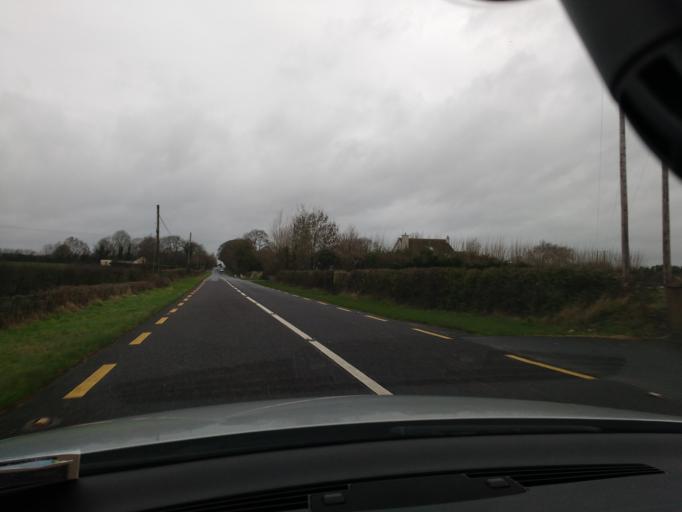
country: IE
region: Munster
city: Thurles
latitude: 52.6724
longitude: -7.7518
